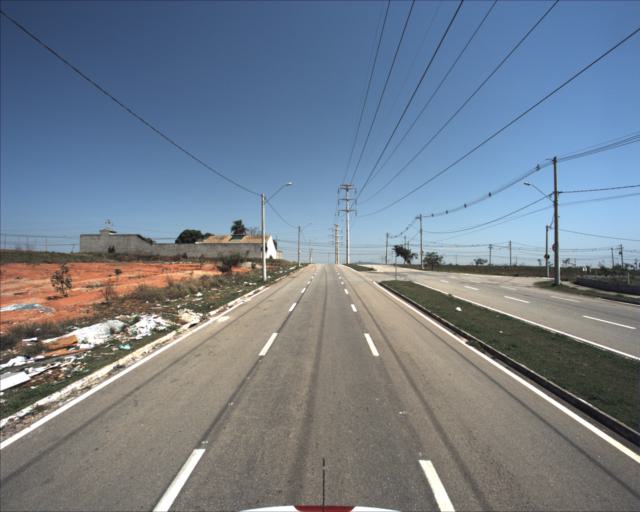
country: BR
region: Sao Paulo
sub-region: Sorocaba
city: Sorocaba
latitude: -23.4465
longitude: -47.5128
